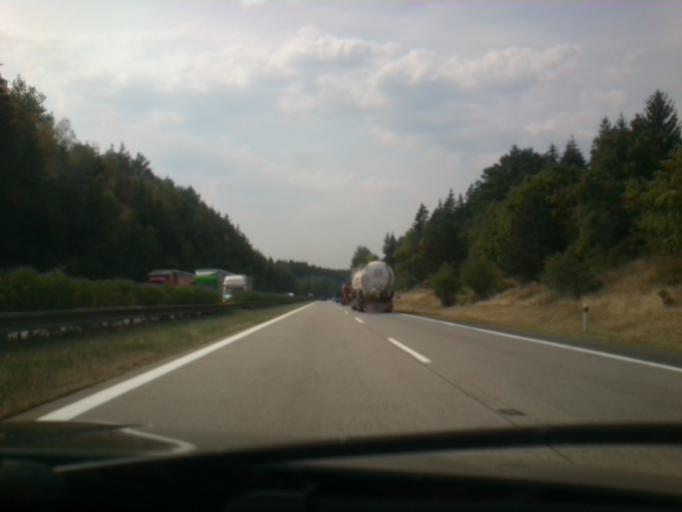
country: CZ
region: Central Bohemia
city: Divisov
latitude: 49.8071
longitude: 14.8937
